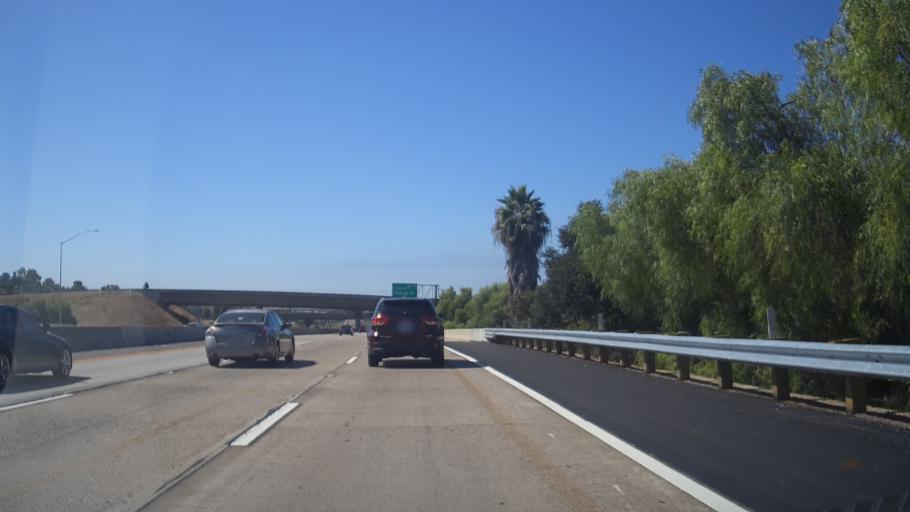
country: US
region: California
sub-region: San Diego County
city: Spring Valley
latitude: 32.7573
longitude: -117.0074
